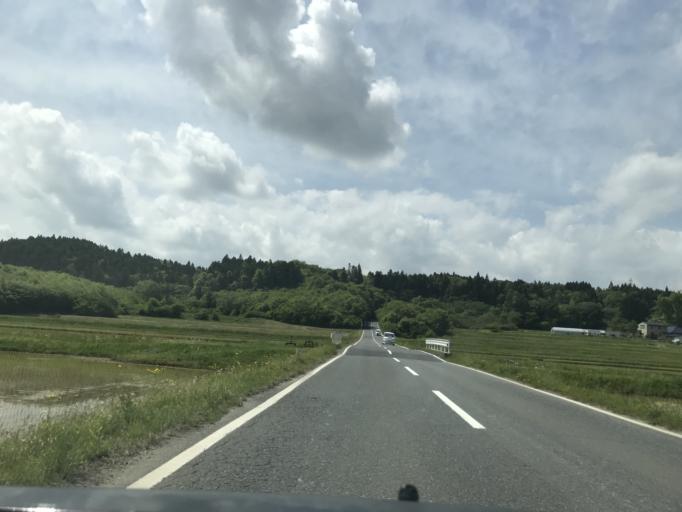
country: JP
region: Iwate
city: Ichinoseki
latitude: 38.7811
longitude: 140.9982
